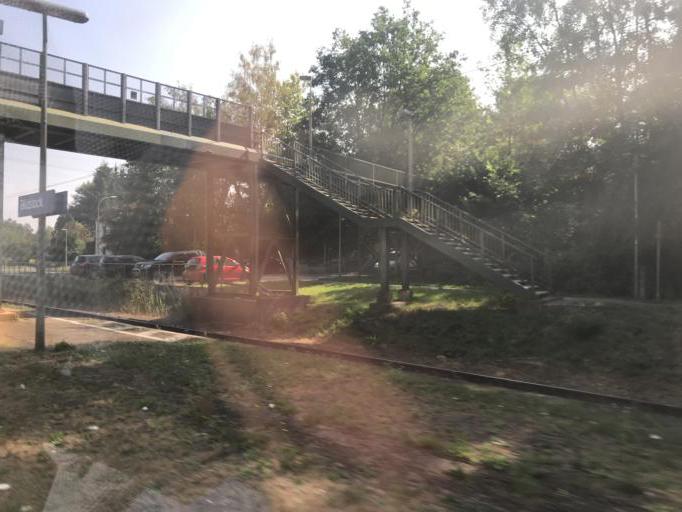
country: DE
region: Saarland
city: Friedrichsthal
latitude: 49.3371
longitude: 7.0939
